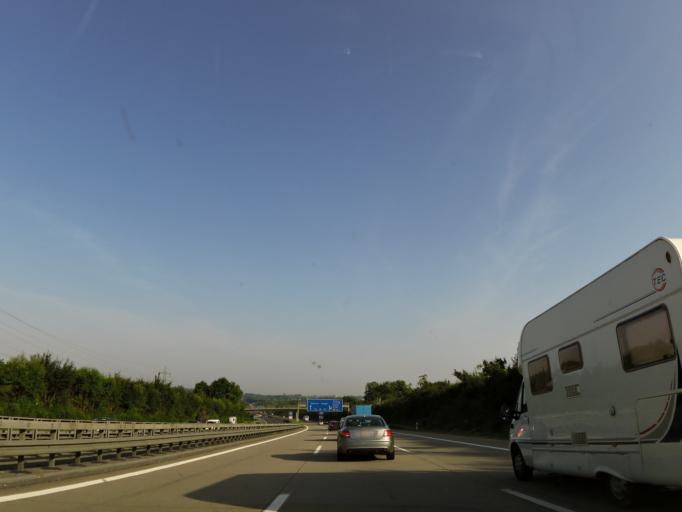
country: DE
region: Baden-Wuerttemberg
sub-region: Regierungsbezirk Stuttgart
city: Wendlingen am Neckar
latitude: 48.6623
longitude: 9.3741
